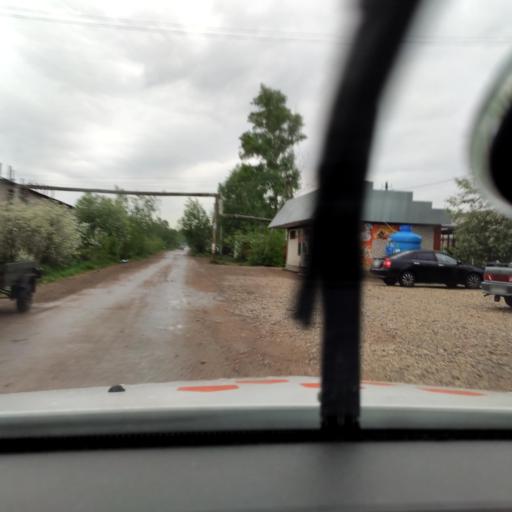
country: RU
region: Bashkortostan
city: Iglino
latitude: 54.8319
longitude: 56.4091
